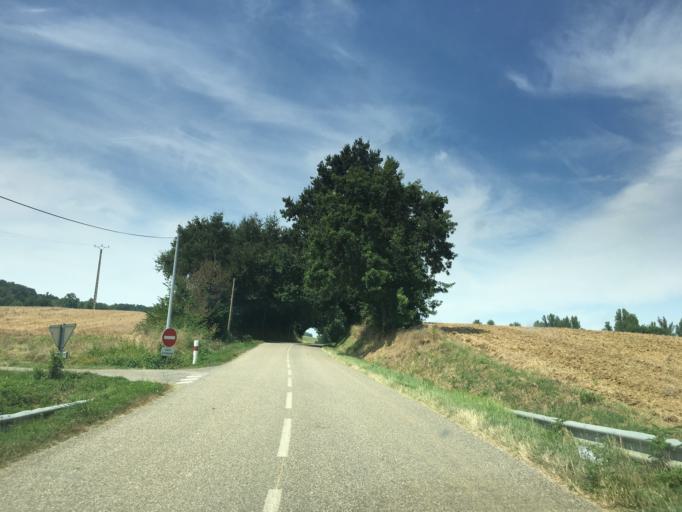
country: FR
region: Midi-Pyrenees
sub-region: Departement du Gers
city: Fleurance
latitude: 43.8968
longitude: 0.7740
